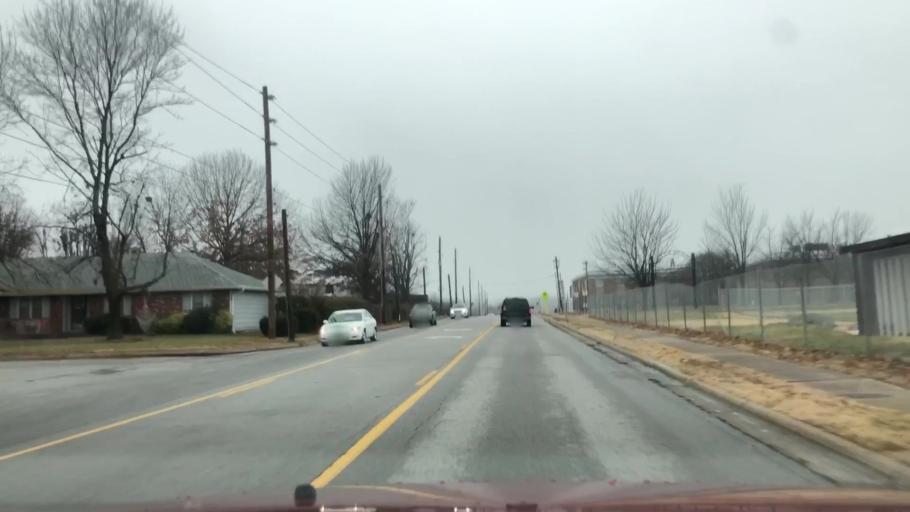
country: US
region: Missouri
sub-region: Greene County
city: Springfield
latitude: 37.1455
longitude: -93.2879
